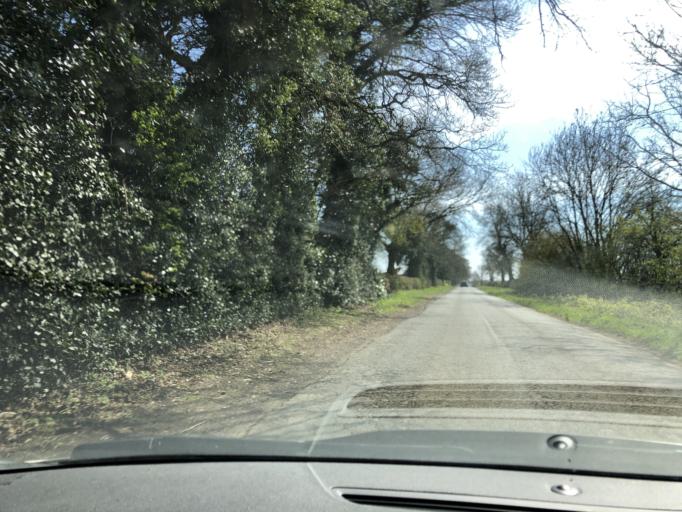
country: GB
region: England
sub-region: Oxfordshire
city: Hook Norton
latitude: 52.0126
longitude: -1.4405
